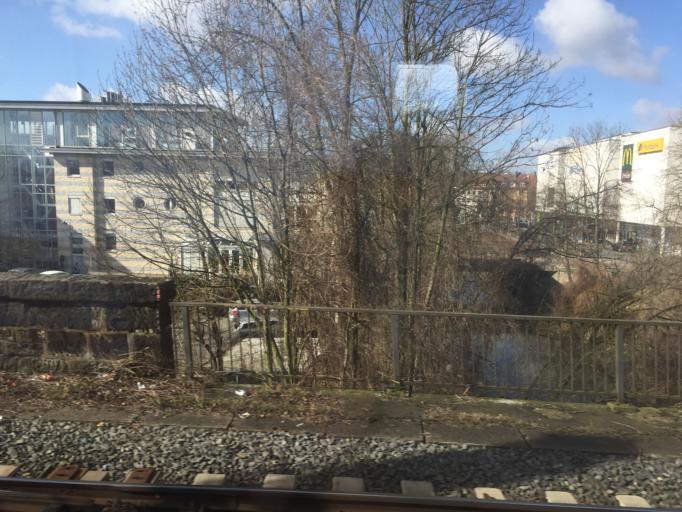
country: DE
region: Lower Saxony
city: Osnabrueck
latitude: 52.2711
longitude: 8.0601
